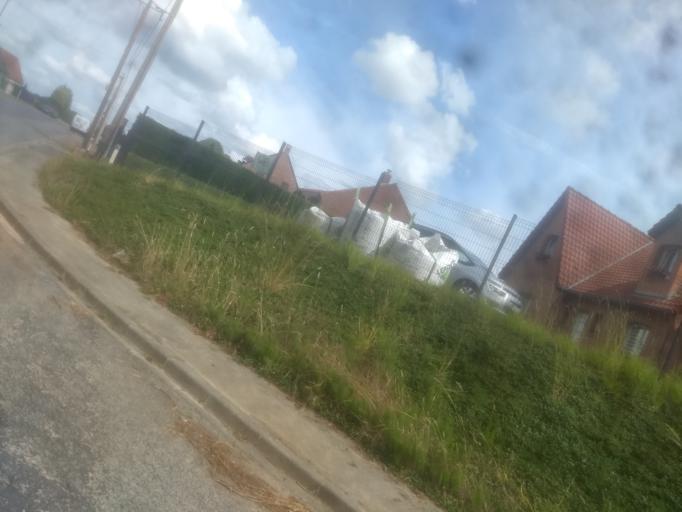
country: FR
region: Nord-Pas-de-Calais
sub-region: Departement du Pas-de-Calais
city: Duisans
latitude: 50.3043
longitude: 2.6793
